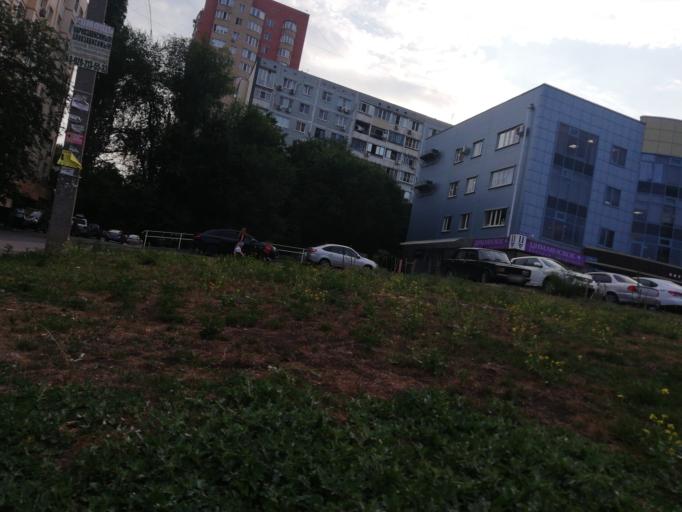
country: RU
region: Rostov
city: Severnyy
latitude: 47.2923
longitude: 39.7139
